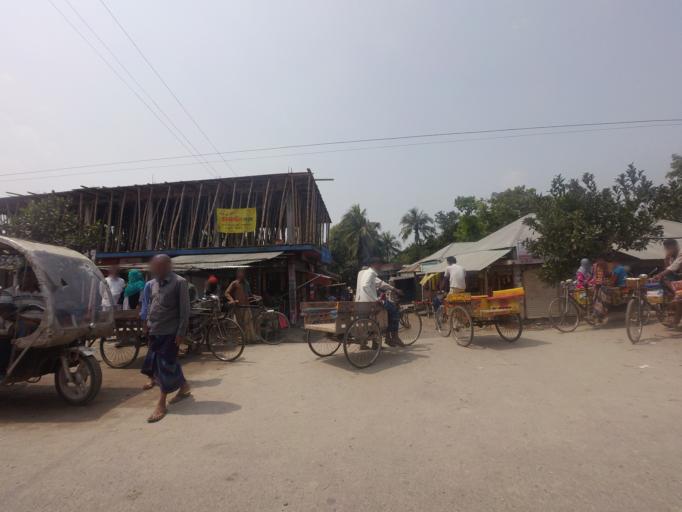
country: BD
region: Rajshahi
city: Sirajganj
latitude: 24.3607
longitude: 89.7064
